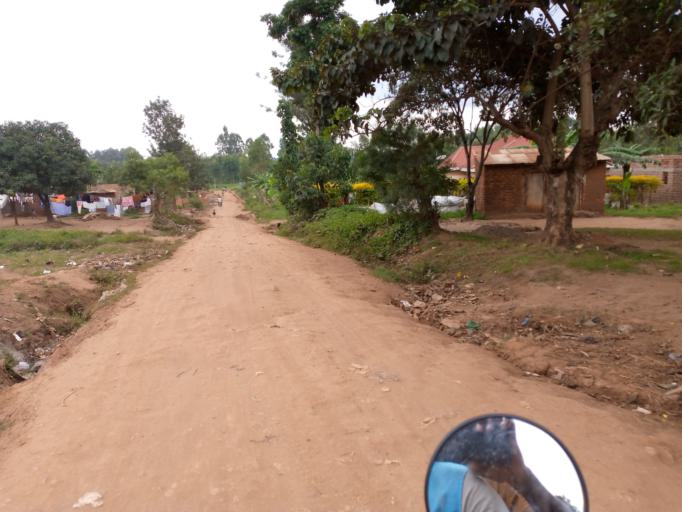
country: UG
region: Eastern Region
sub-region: Mbale District
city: Mbale
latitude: 1.0884
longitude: 34.1640
